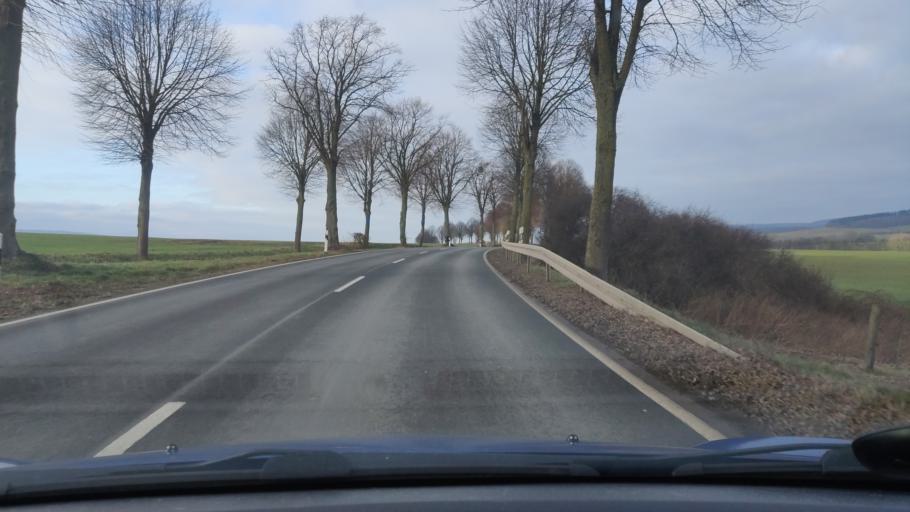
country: DE
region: Lower Saxony
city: Bad Munder am Deister
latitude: 52.1523
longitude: 9.4929
